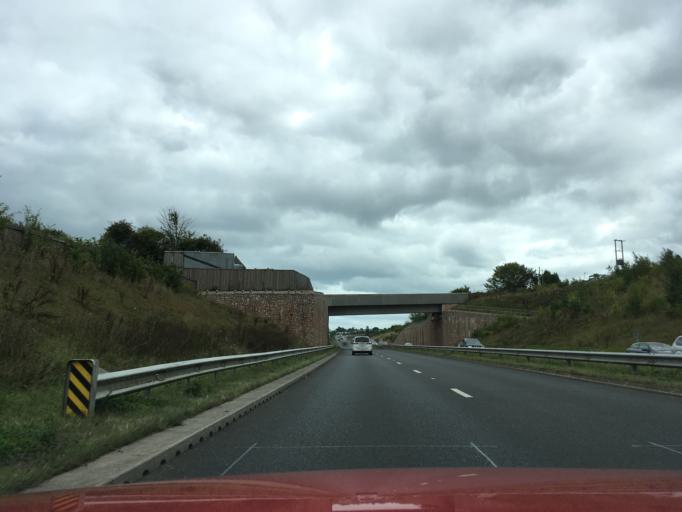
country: GB
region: England
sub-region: Devon
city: Kingskerswell
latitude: 50.4956
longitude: -3.5862
